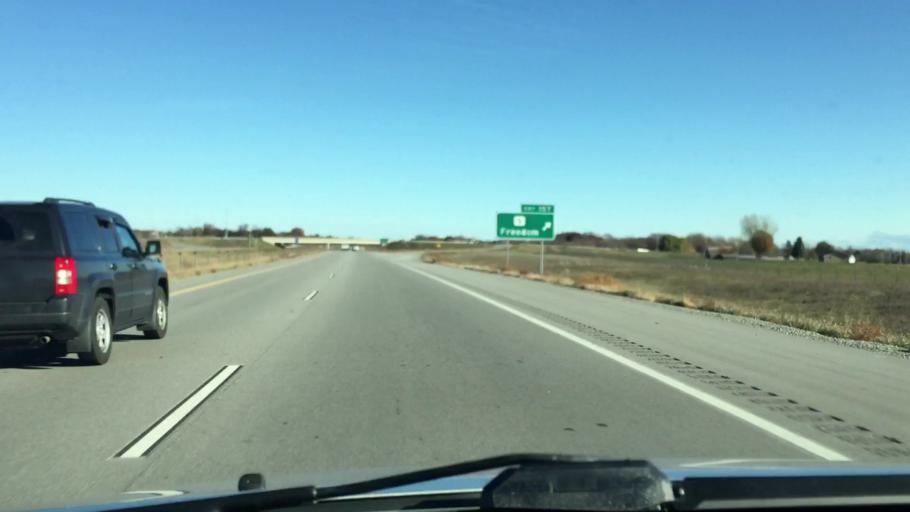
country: US
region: Wisconsin
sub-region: Brown County
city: Wrightstown
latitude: 44.3817
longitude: -88.1646
